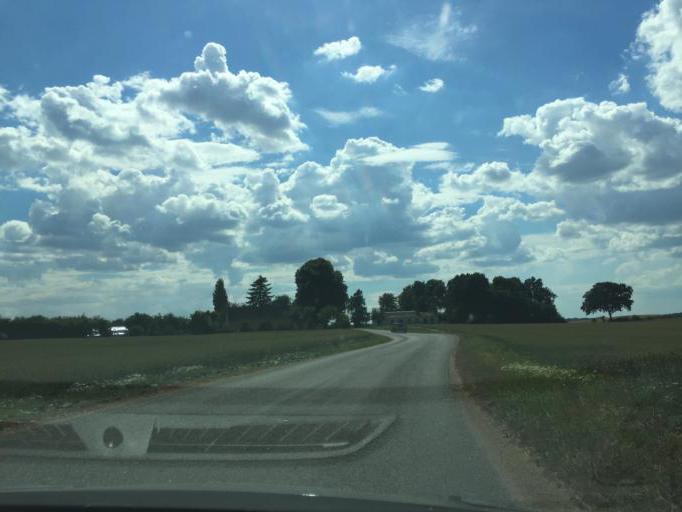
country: DK
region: South Denmark
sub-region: Odense Kommune
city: Bellinge
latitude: 55.2426
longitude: 10.2840
